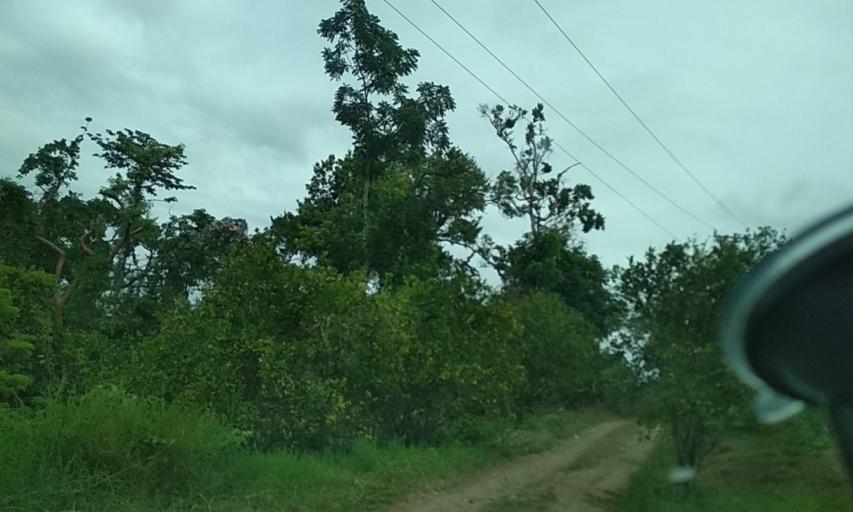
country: MX
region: Veracruz
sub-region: Papantla
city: Residencial Tajin
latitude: 20.6160
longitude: -97.3529
